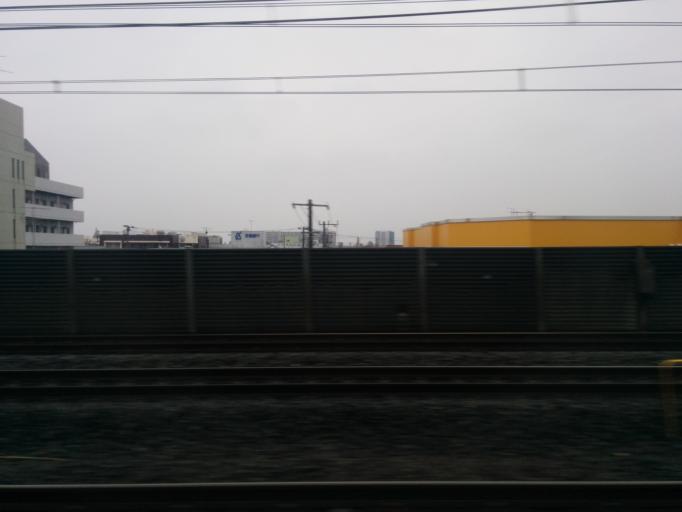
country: JP
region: Chiba
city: Chiba
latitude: 35.6265
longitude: 140.1001
